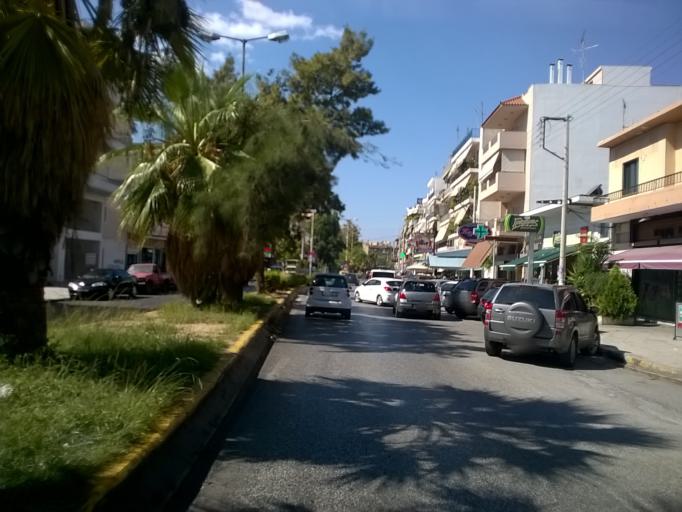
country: GR
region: Attica
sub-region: Nomos Piraios
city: Keratsini
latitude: 37.9642
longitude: 23.6321
